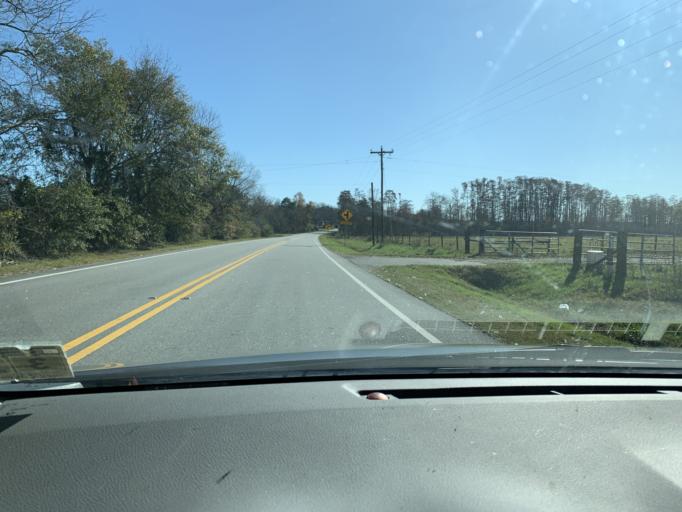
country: US
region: Georgia
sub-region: Ben Hill County
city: Fitzgerald
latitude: 31.7134
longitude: -83.1721
